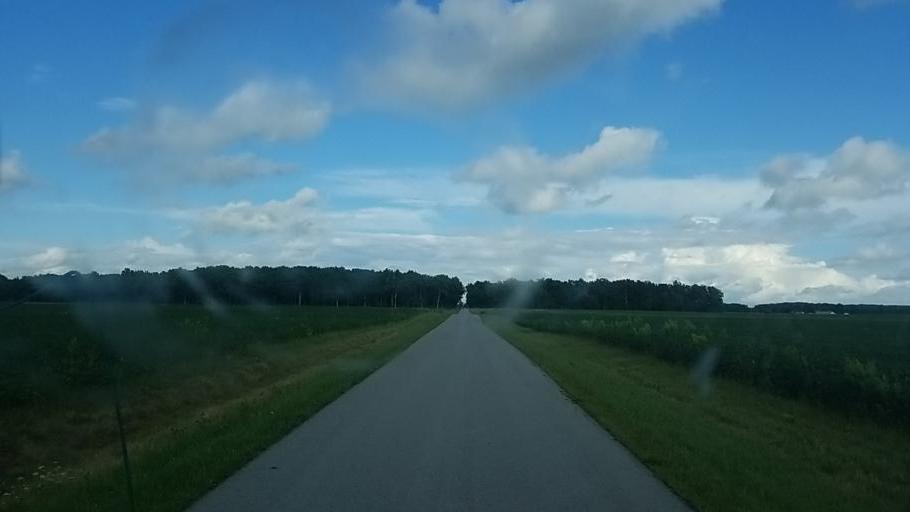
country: US
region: Ohio
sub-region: Hardin County
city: Forest
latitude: 40.7597
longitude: -83.4748
